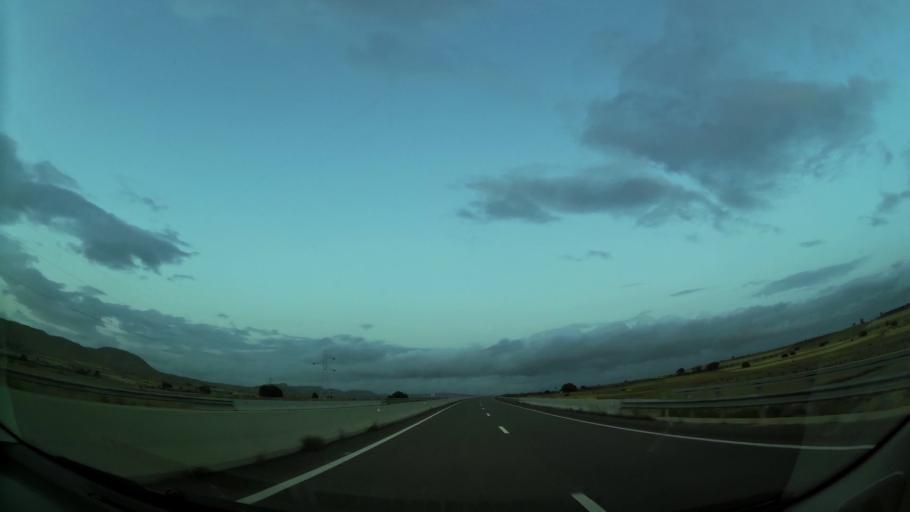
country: MA
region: Oriental
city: El Aioun
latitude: 34.6241
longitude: -2.5028
